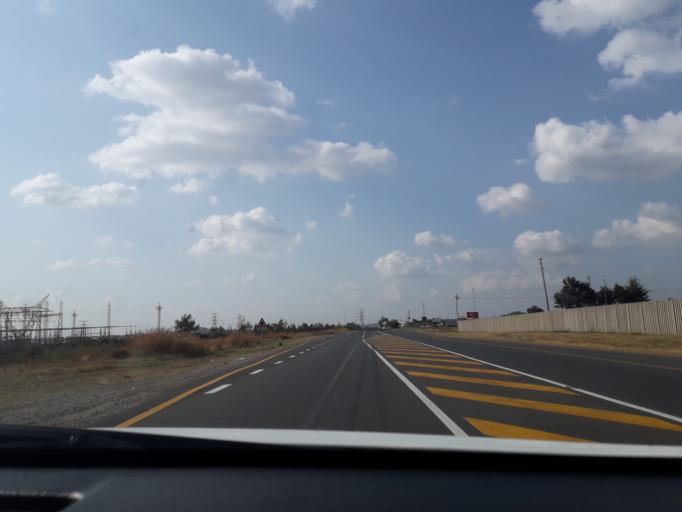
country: ZA
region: Gauteng
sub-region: City of Tshwane Metropolitan Municipality
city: Centurion
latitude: -25.8991
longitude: 28.2478
